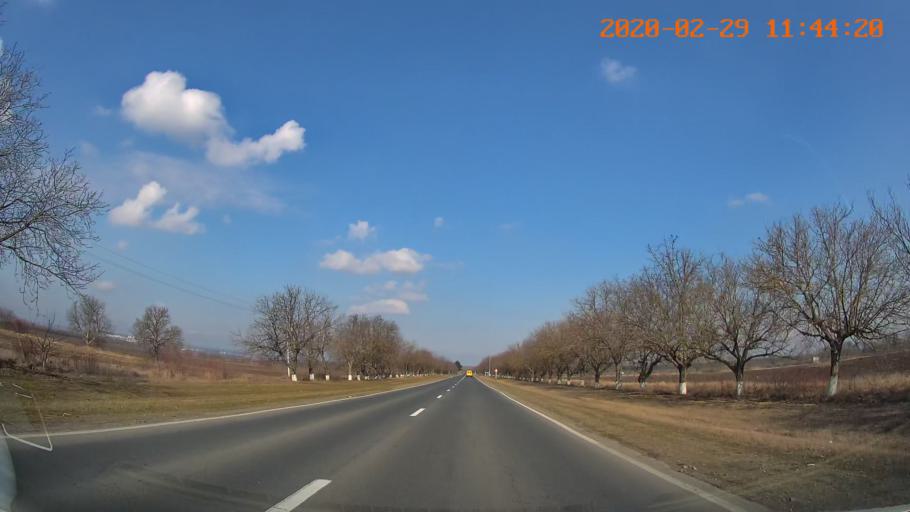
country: MD
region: Rezina
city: Saharna
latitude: 47.7098
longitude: 29.0009
